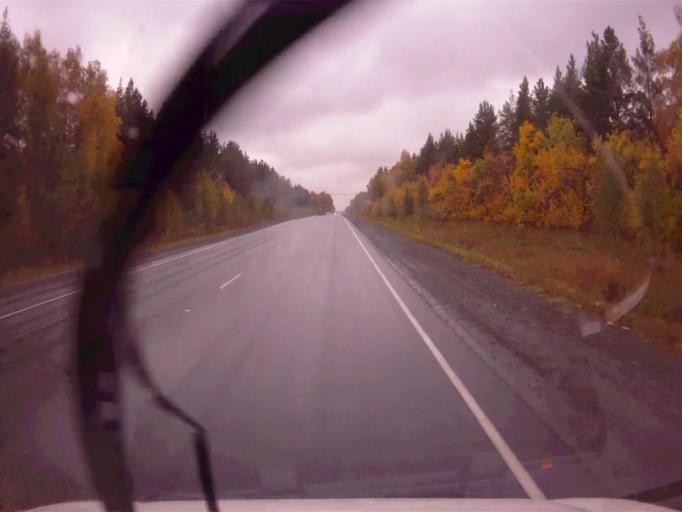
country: RU
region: Chelyabinsk
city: Roshchino
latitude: 55.3794
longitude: 61.1438
